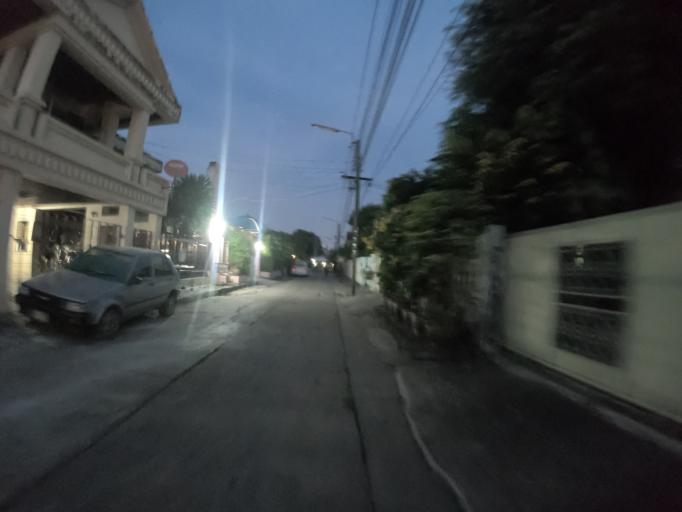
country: TH
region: Bangkok
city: Lat Phrao
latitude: 13.8263
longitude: 100.6114
